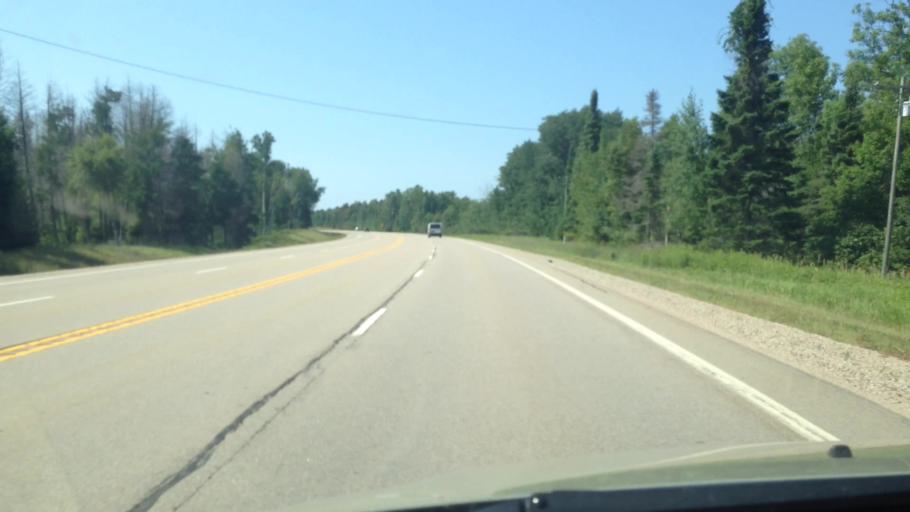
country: US
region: Michigan
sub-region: Delta County
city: Escanaba
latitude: 45.5343
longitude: -87.2845
